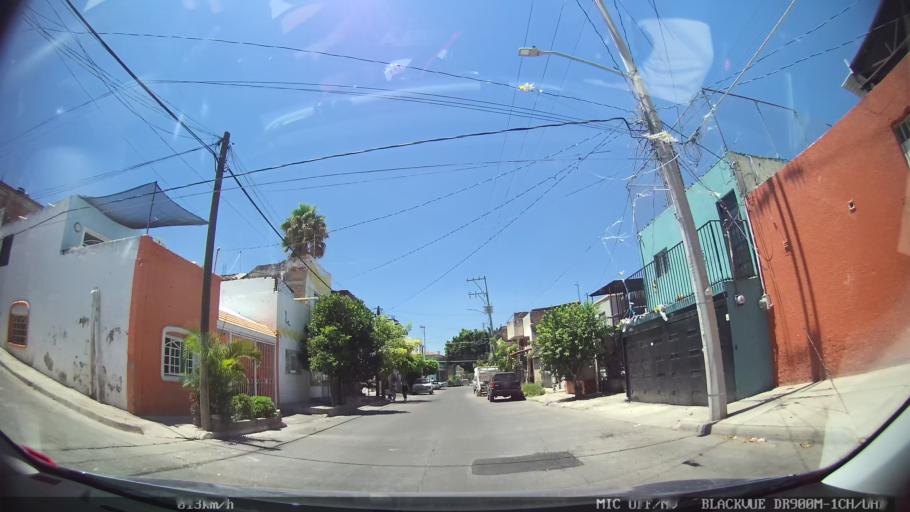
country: MX
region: Jalisco
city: Tlaquepaque
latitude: 20.6626
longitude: -103.2721
